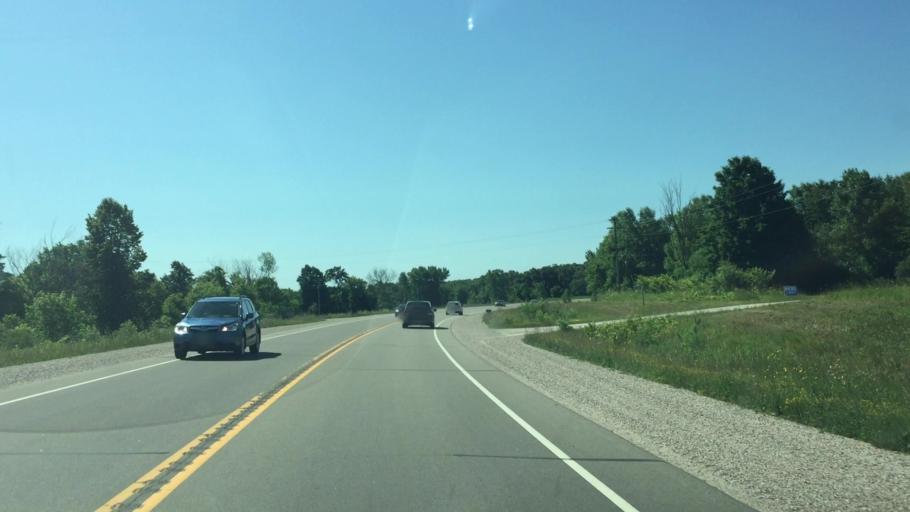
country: US
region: Wisconsin
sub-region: Calumet County
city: New Holstein
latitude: 43.9804
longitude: -88.1135
